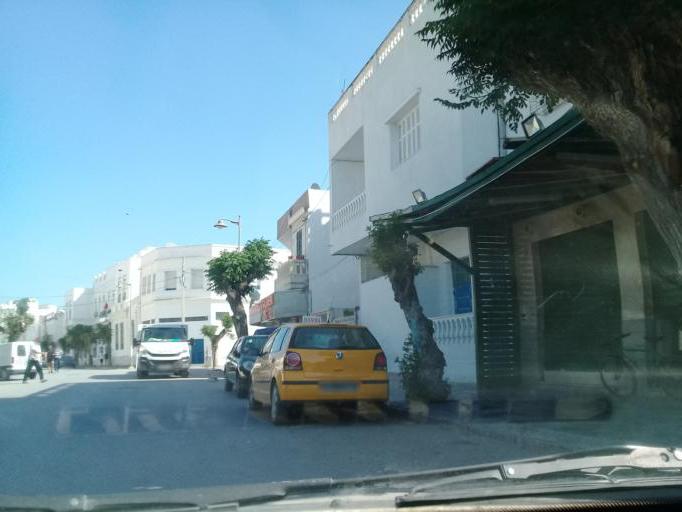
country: TN
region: Tunis
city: La Goulette
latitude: 36.8170
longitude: 10.3021
